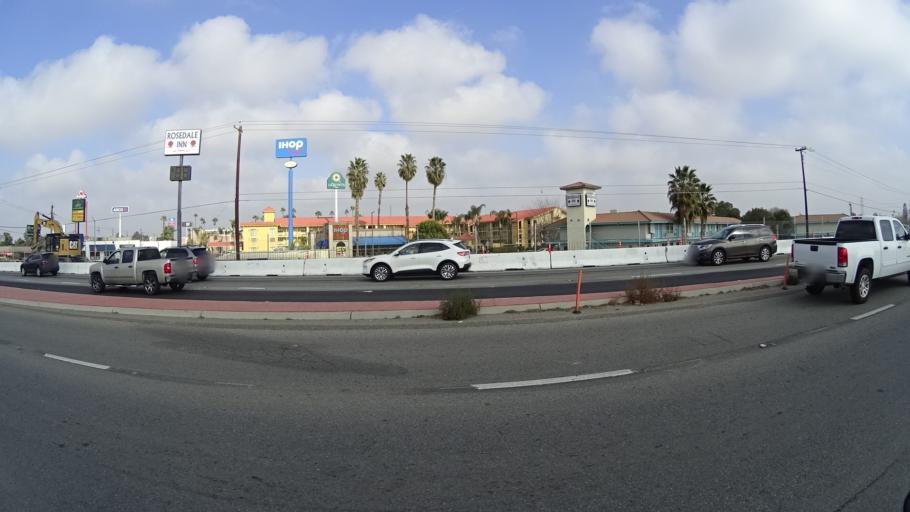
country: US
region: California
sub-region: Kern County
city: Bakersfield
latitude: 35.3826
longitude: -119.0425
